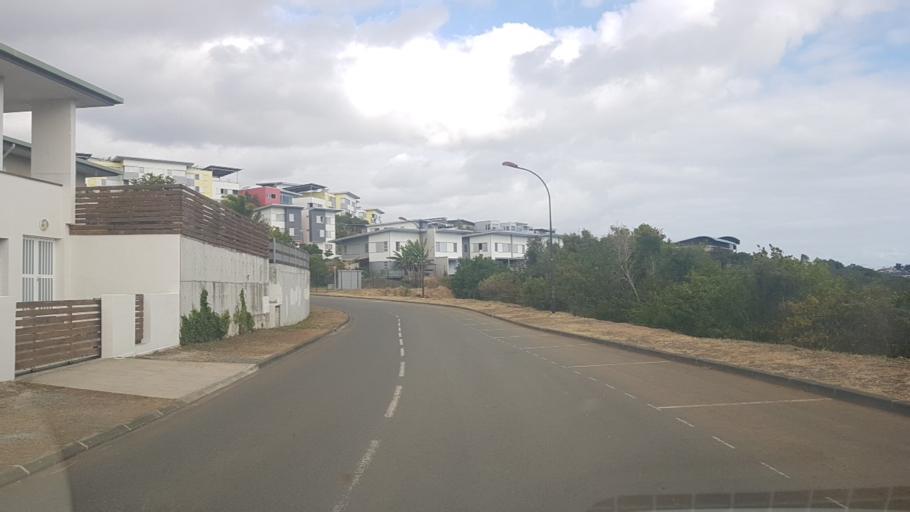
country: NC
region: South Province
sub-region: Dumbea
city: Dumbea
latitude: -22.2067
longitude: 166.4480
